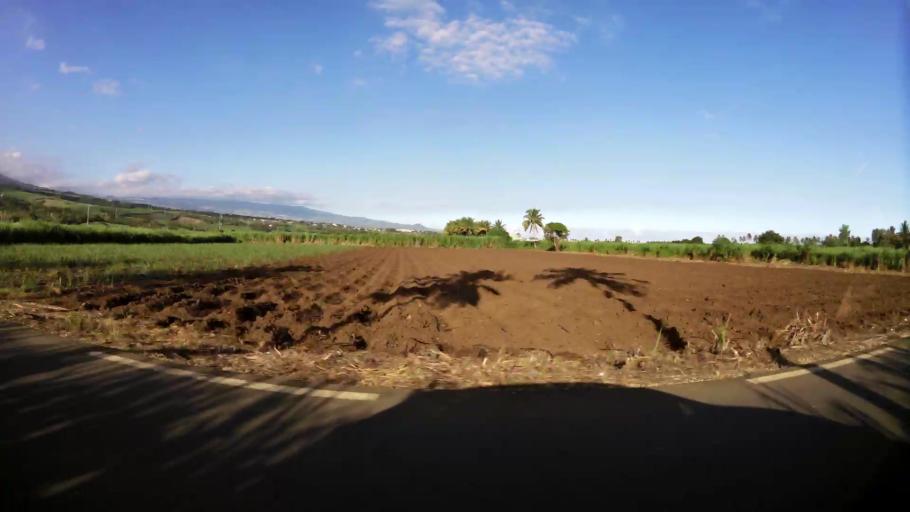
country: RE
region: Reunion
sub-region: Reunion
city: Saint-Louis
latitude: -21.2687
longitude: 55.3785
